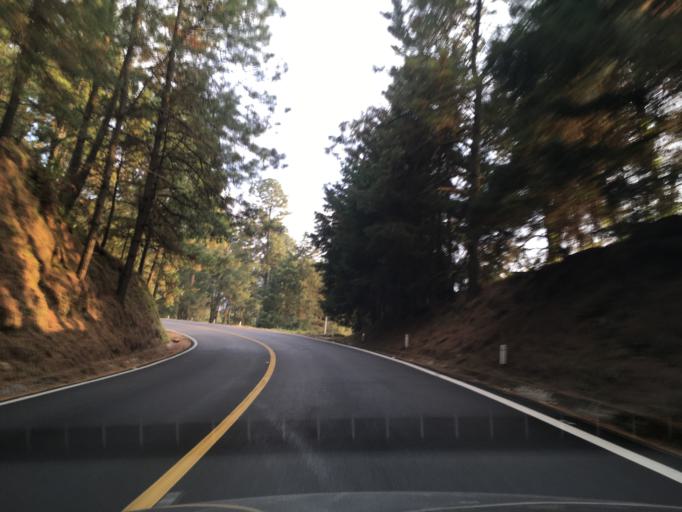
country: MX
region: Michoacan
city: Tingambato
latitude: 19.4973
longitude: -101.8271
